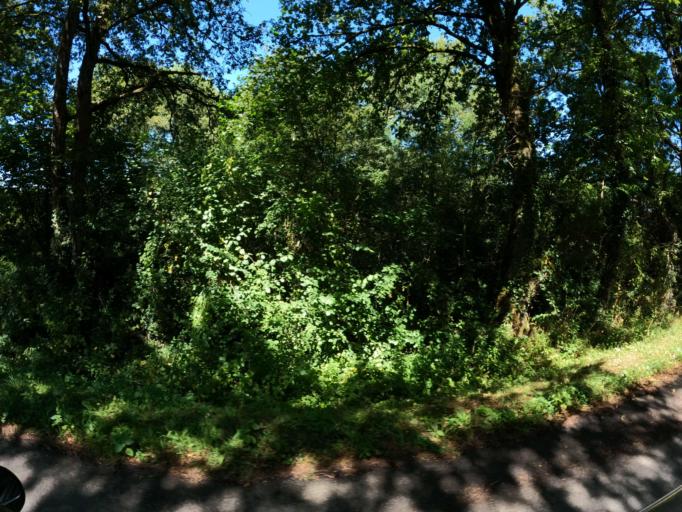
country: FR
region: Pays de la Loire
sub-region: Departement de la Loire-Atlantique
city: La Limouziniere
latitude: 46.9693
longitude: -1.5719
